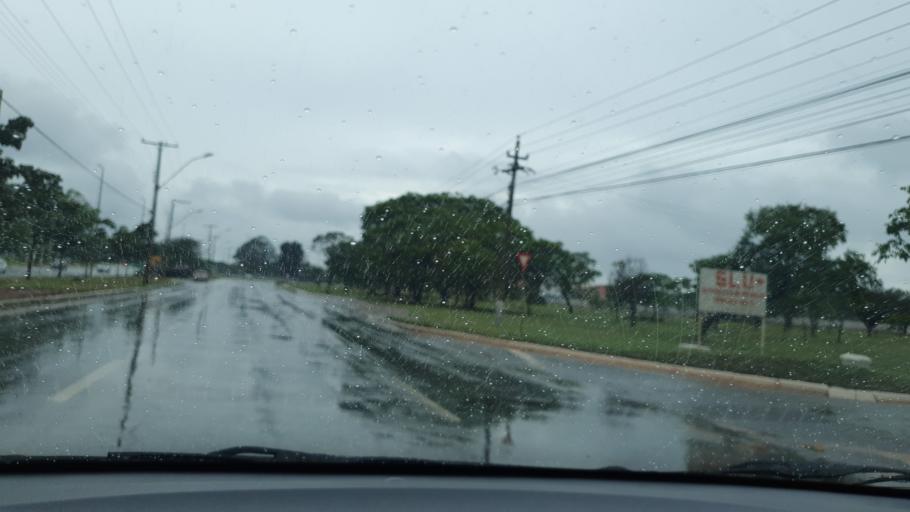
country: BR
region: Federal District
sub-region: Brasilia
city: Brasilia
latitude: -15.7690
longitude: -47.9120
